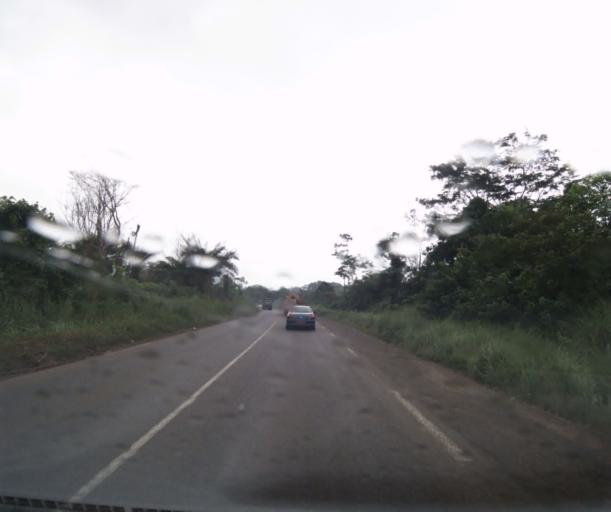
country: CM
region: Littoral
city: Edea
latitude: 3.7903
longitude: 10.2067
